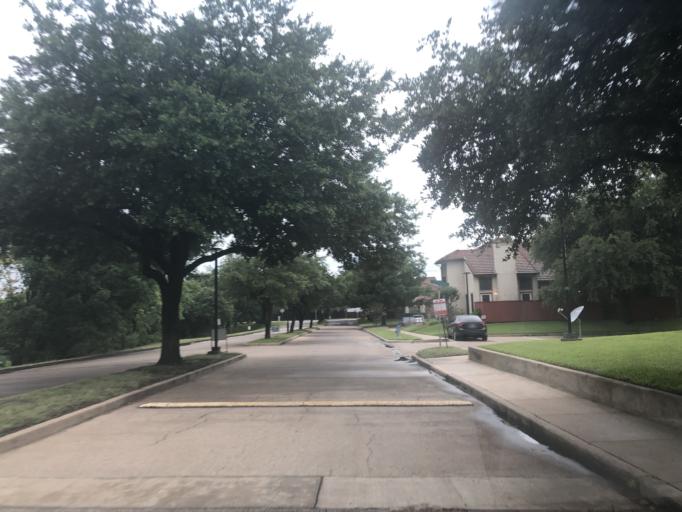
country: US
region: Texas
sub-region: Dallas County
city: Irving
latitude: 32.7907
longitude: -96.9580
